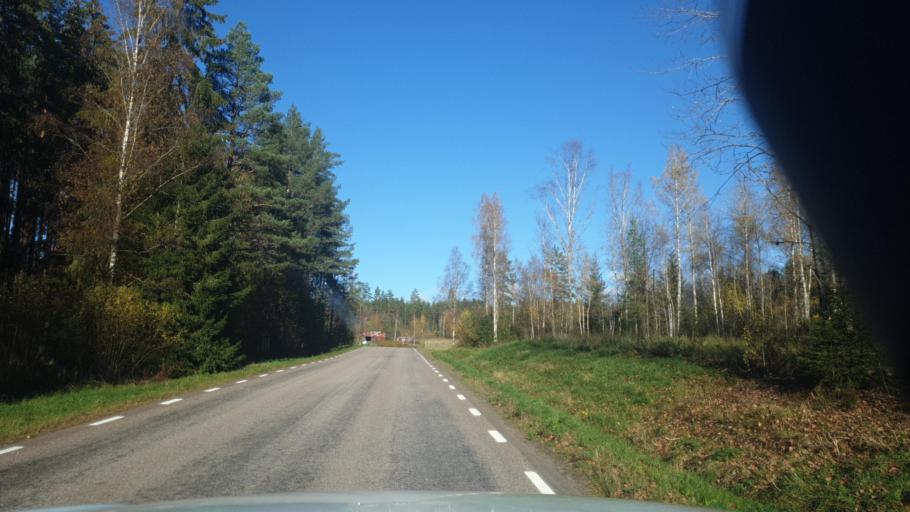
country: SE
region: Vaermland
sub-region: Arvika Kommun
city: Arvika
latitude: 59.6190
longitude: 12.7886
